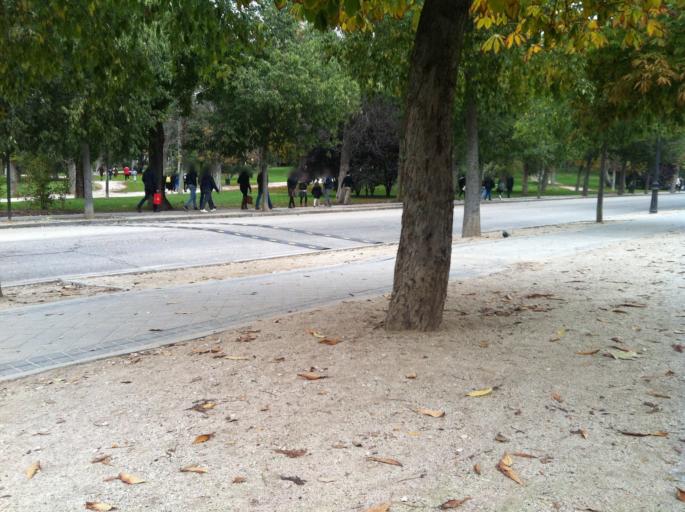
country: ES
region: Madrid
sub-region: Provincia de Madrid
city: Retiro
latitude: 40.4096
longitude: -3.6883
